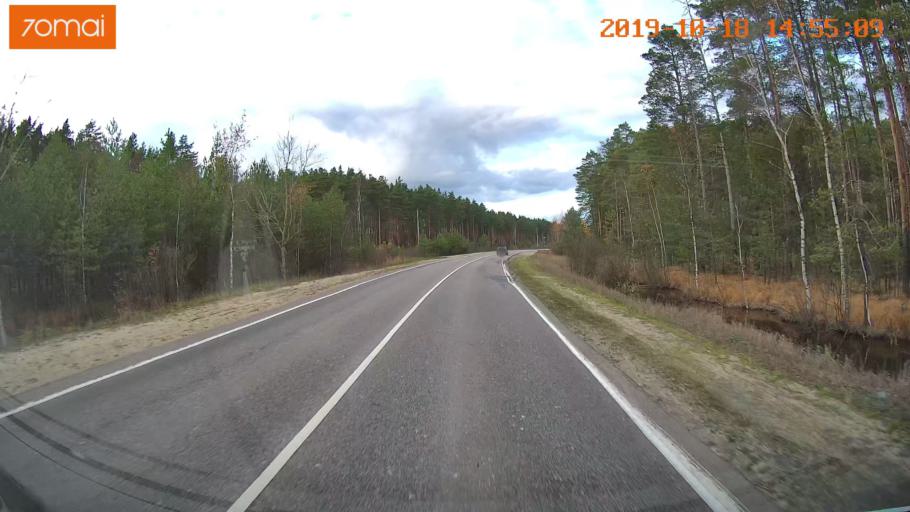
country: RU
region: Vladimir
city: Kurlovo
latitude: 55.4481
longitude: 40.5889
